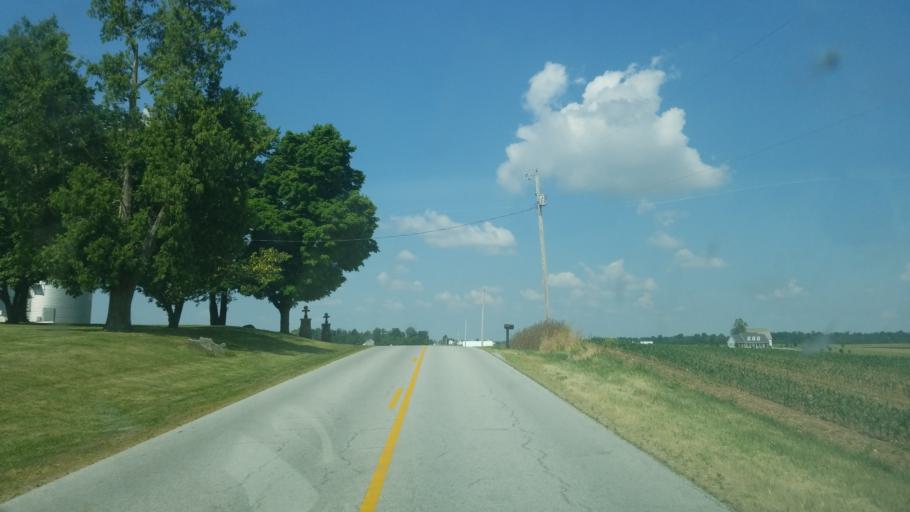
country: US
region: Ohio
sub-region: Auglaize County
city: Wapakoneta
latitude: 40.5705
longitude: -84.1226
